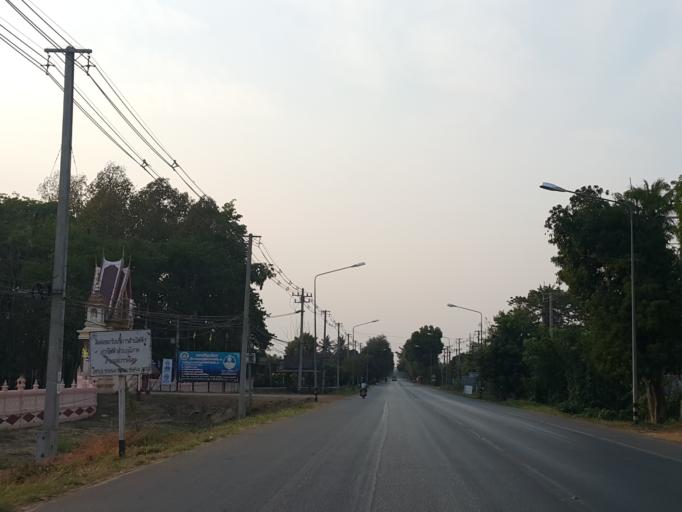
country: TH
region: Sukhothai
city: Si Samrong
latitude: 17.2136
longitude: 99.8654
